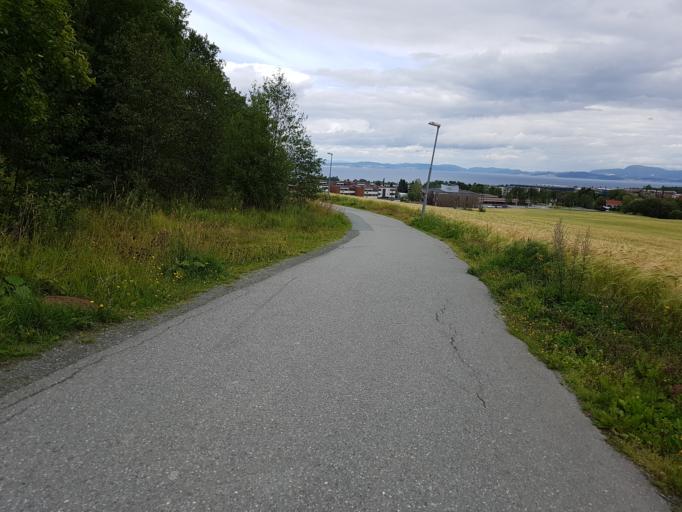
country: NO
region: Sor-Trondelag
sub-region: Trondheim
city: Trondheim
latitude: 63.4151
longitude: 10.4731
